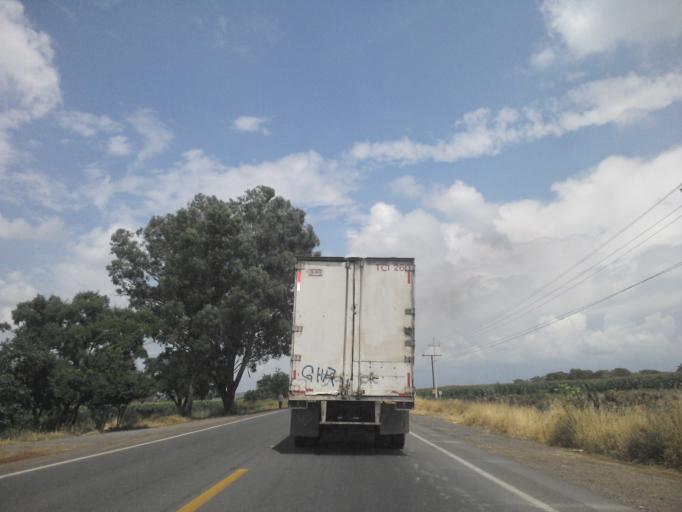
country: MX
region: Jalisco
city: Acatic
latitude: 20.7028
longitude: -102.9692
